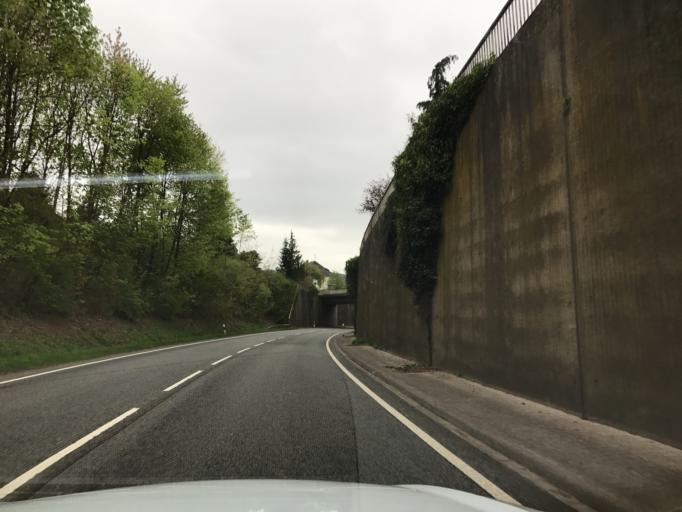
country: DE
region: Rheinland-Pfalz
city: Ockfen
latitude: 49.6044
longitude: 6.5666
